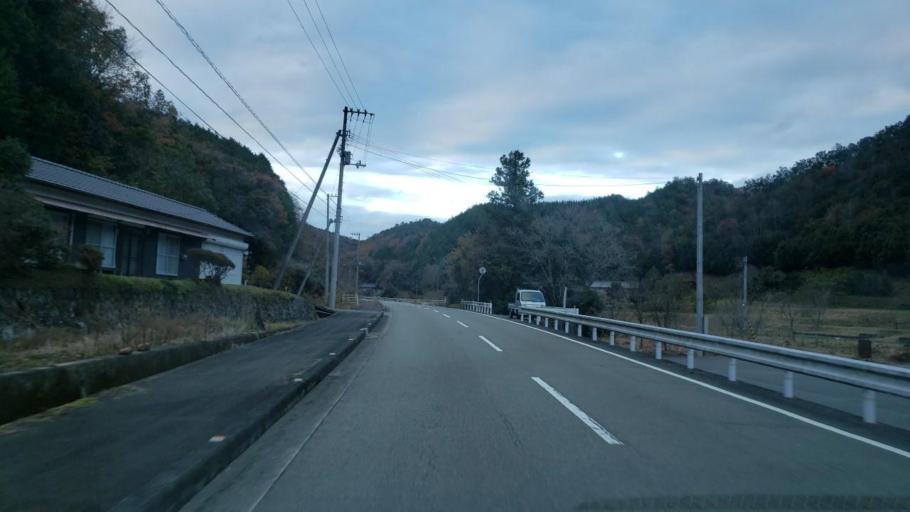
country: JP
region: Tokushima
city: Kamojimacho-jogejima
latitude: 34.1868
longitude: 134.2514
